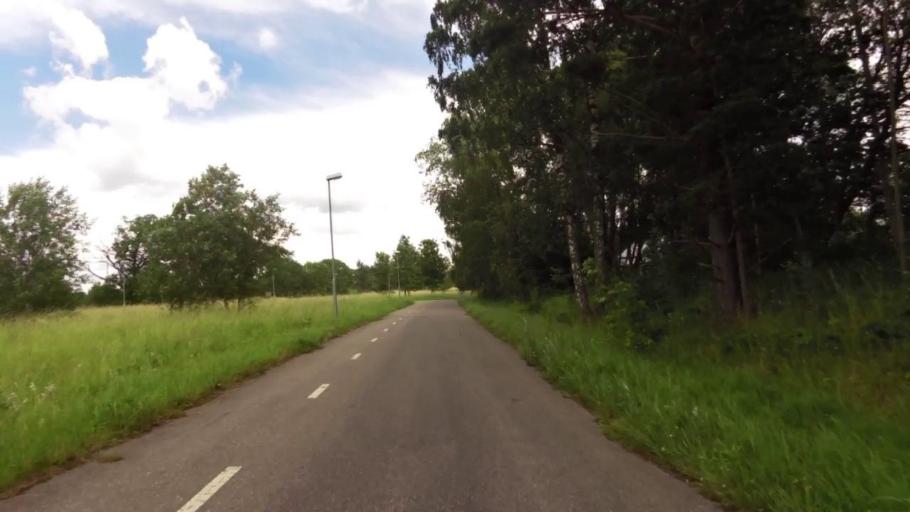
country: SE
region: OEstergoetland
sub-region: Linkopings Kommun
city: Malmslatt
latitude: 58.4028
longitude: 15.5571
